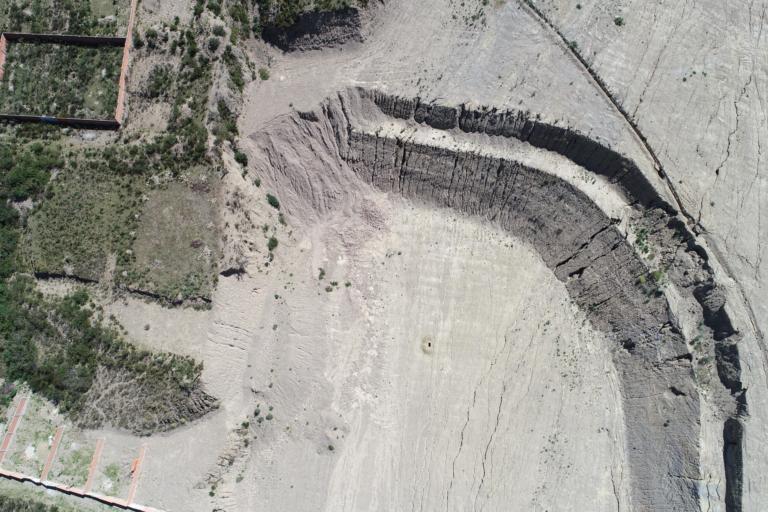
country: BO
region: La Paz
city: La Paz
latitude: -16.5062
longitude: -68.0577
